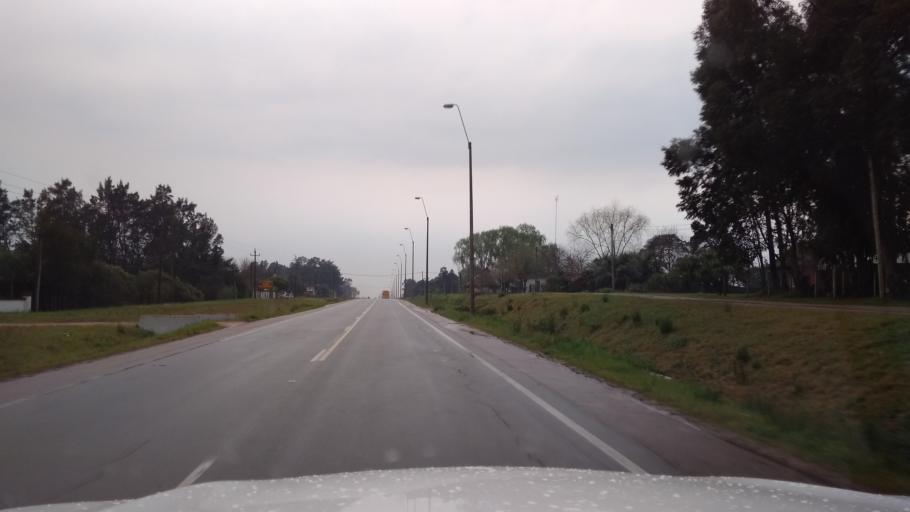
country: UY
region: Canelones
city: Toledo
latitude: -34.7635
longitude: -56.1184
